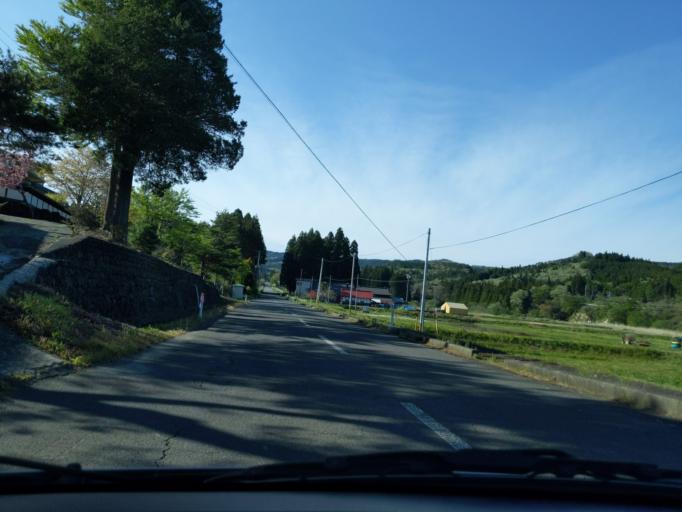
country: JP
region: Iwate
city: Ichinoseki
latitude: 38.8623
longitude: 140.9067
